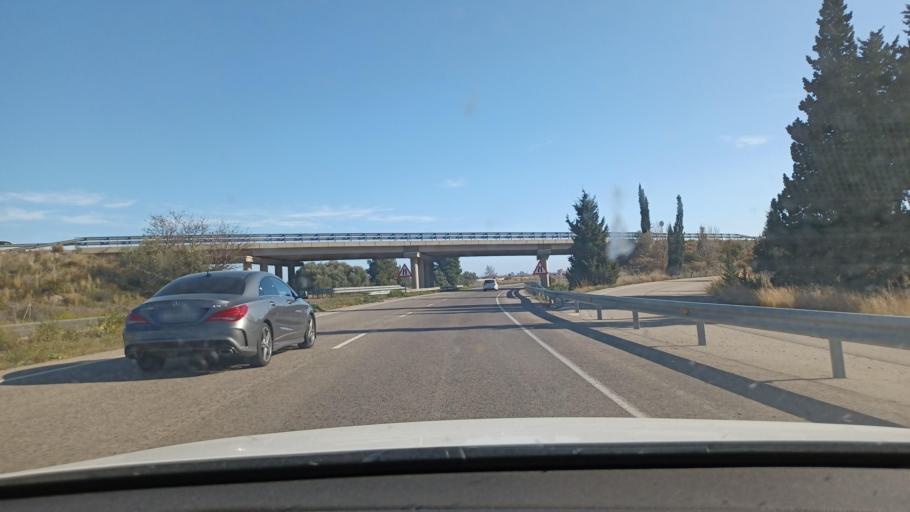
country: ES
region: Catalonia
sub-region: Provincia de Tarragona
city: Amposta
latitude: 40.7258
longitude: 0.5897
